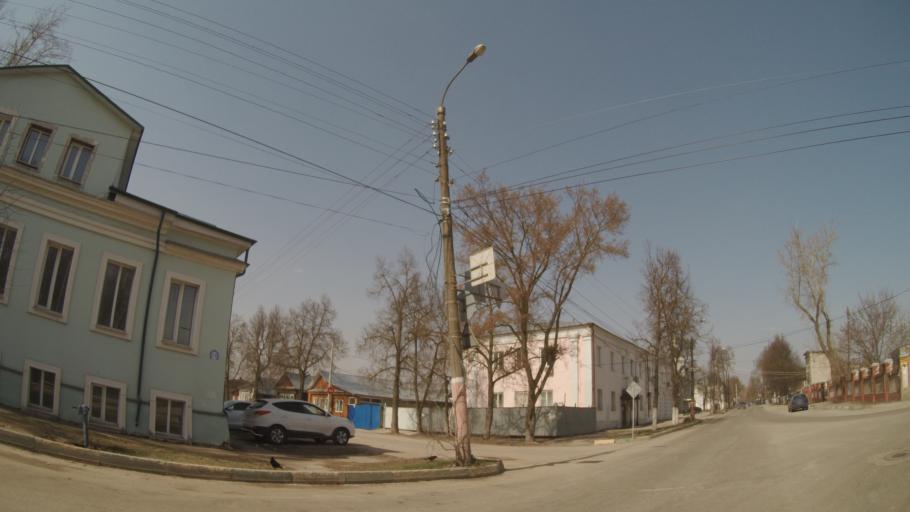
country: RU
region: Nizjnij Novgorod
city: Arzamas
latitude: 55.3880
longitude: 43.8132
